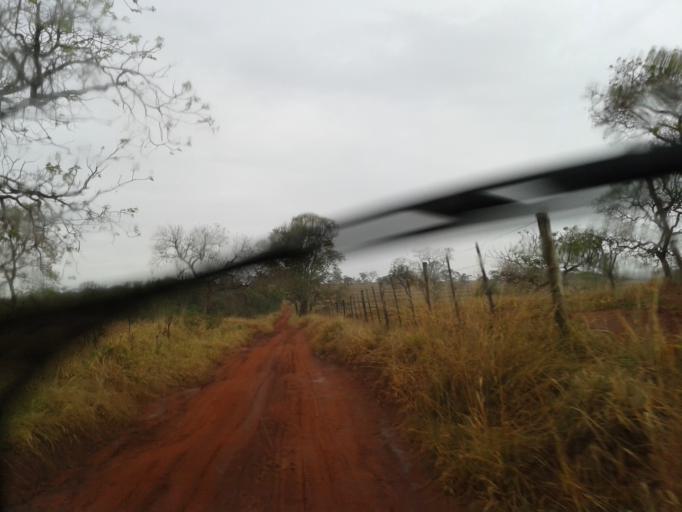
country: BR
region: Minas Gerais
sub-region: Campina Verde
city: Campina Verde
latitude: -19.3548
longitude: -49.5390
